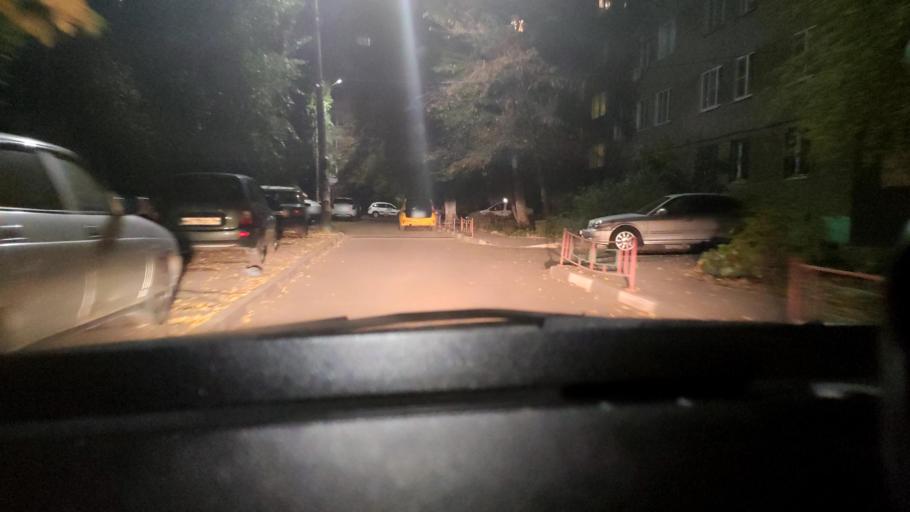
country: RU
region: Voronezj
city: Podgornoye
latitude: 51.7043
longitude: 39.1500
